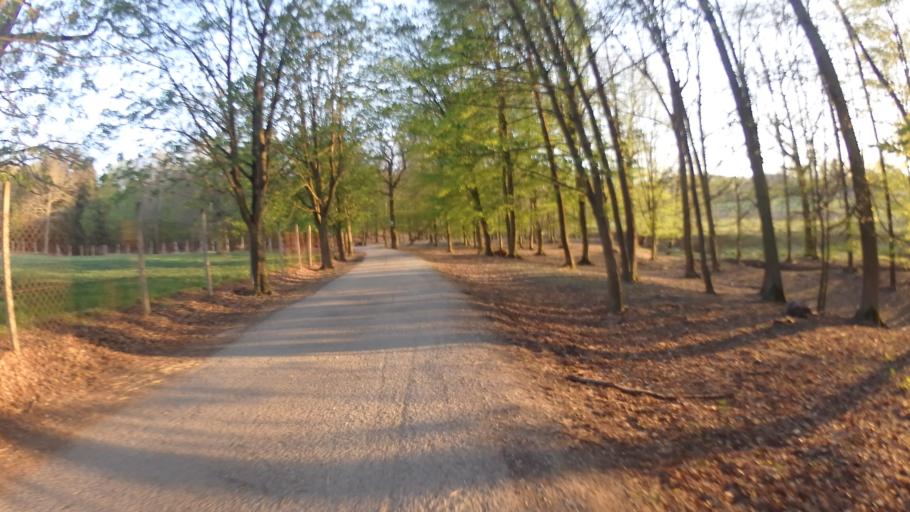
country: CZ
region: South Moravian
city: Troubsko
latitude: 49.2068
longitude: 16.5235
